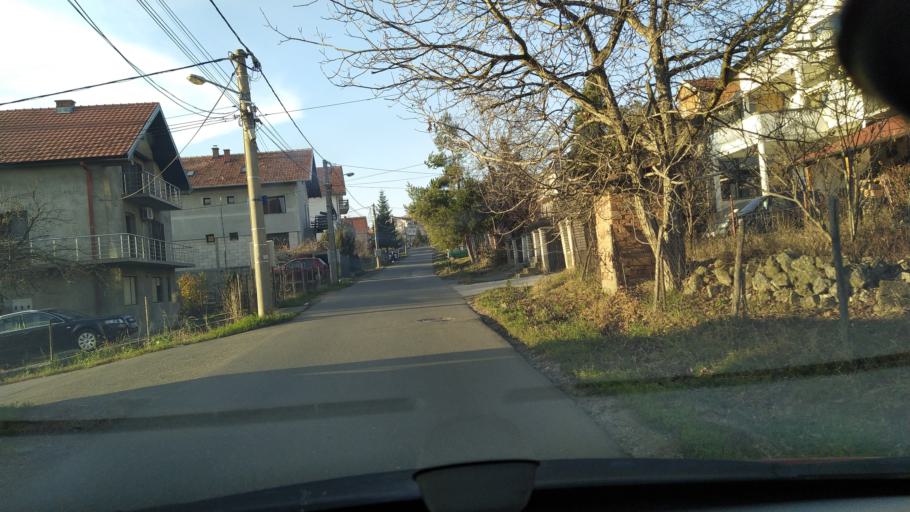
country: RS
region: Central Serbia
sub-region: Belgrade
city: Zvezdara
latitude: 44.7521
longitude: 20.5713
